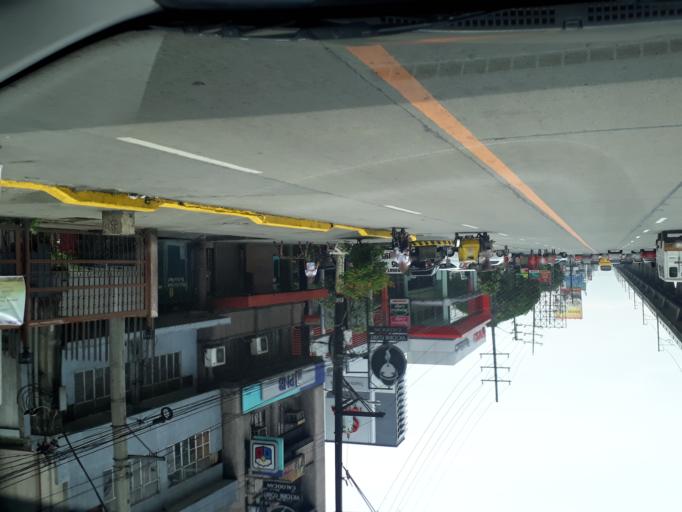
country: PH
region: Calabarzon
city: Del Monte
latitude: 14.6575
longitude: 120.9968
